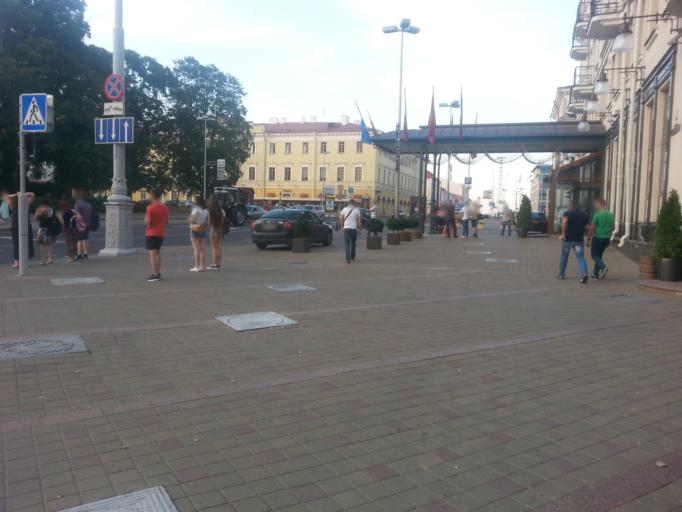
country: BY
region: Minsk
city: Minsk
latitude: 53.9026
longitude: 27.5567
